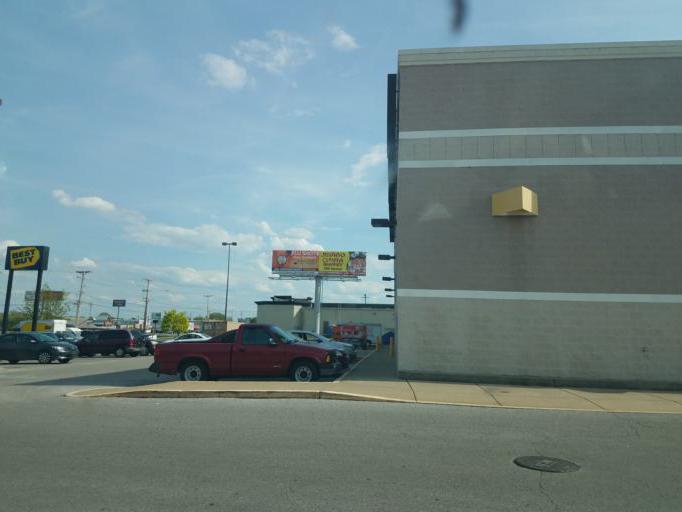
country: US
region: Kentucky
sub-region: Warren County
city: Bowling Green
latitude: 36.9539
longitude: -86.4276
